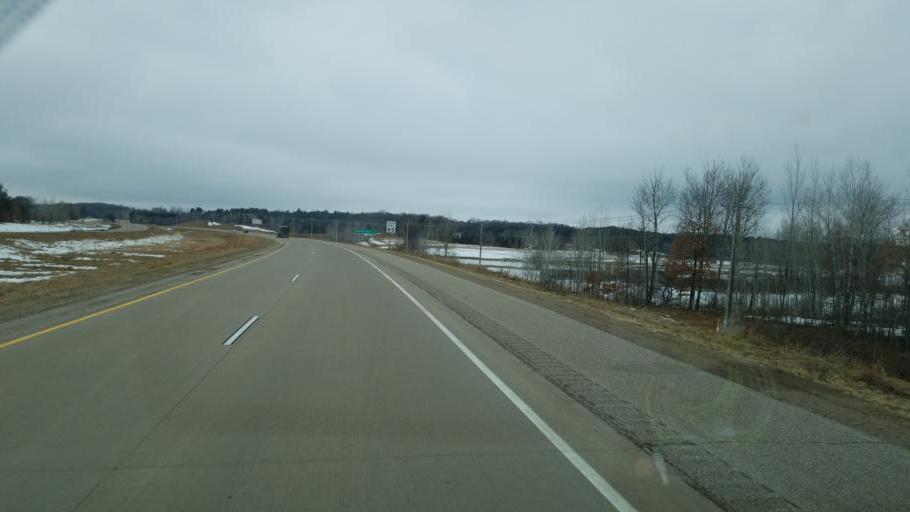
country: US
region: Wisconsin
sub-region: Portage County
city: Amherst
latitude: 44.4998
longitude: -89.3765
